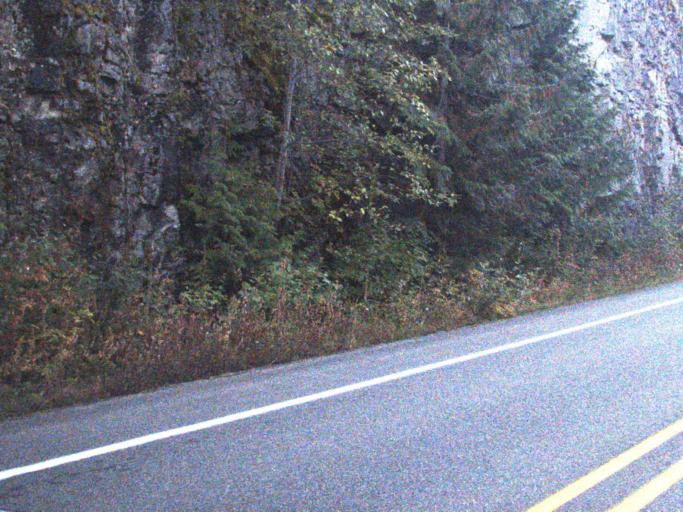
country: US
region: Washington
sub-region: Snohomish County
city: Darrington
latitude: 48.7113
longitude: -120.9892
